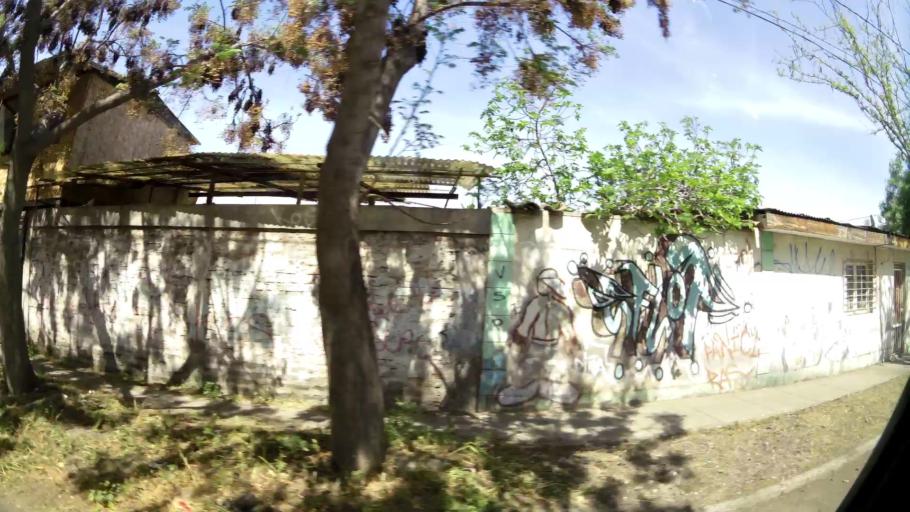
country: CL
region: Santiago Metropolitan
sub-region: Provincia de Santiago
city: Lo Prado
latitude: -33.4268
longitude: -70.7353
